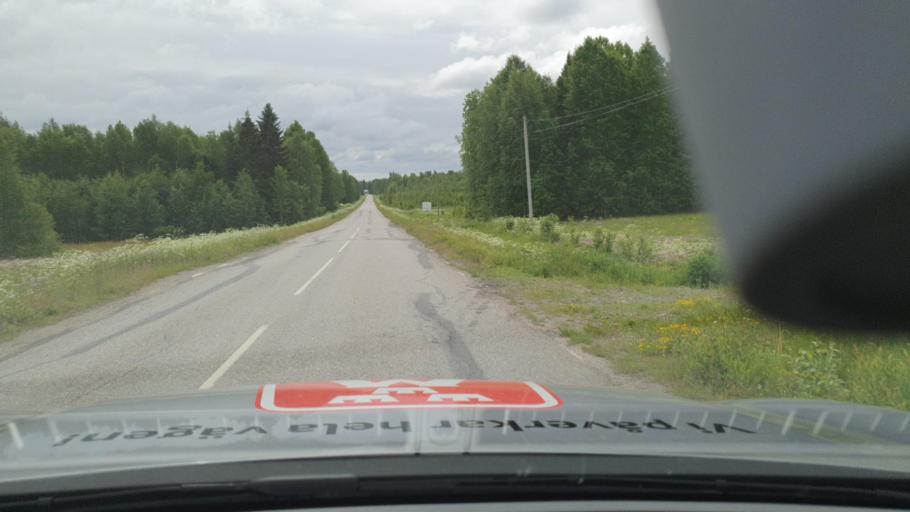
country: SE
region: Norrbotten
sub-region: Lulea Kommun
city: Ranea
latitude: 65.9280
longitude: 22.1436
